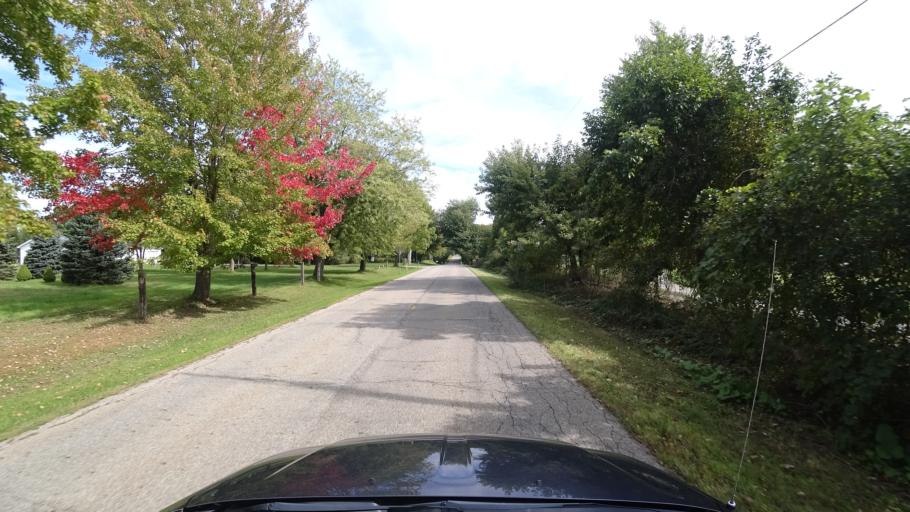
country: US
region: Indiana
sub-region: LaPorte County
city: Trail Creek
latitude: 41.7091
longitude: -86.8393
